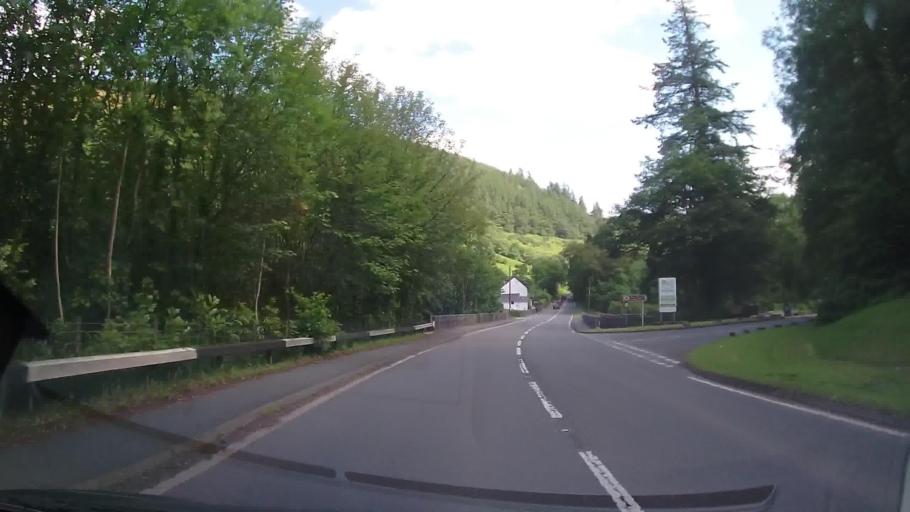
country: GB
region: Wales
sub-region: Gwynedd
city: Corris
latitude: 52.7117
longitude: -3.6899
